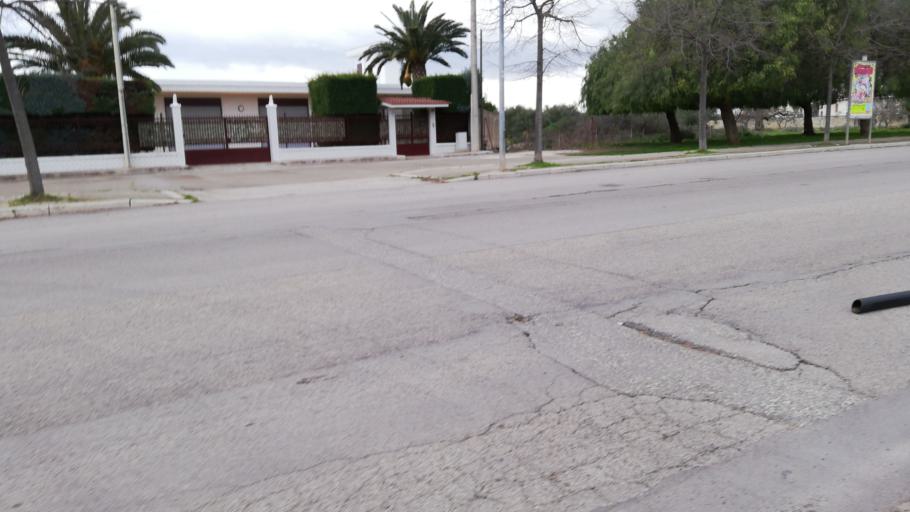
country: IT
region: Apulia
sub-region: Provincia di Bari
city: Bitonto
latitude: 41.1134
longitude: 16.6822
